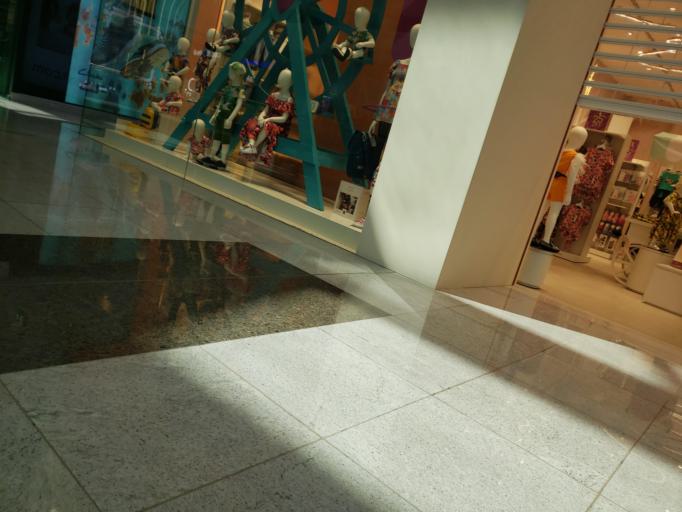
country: AE
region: Dubai
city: Dubai
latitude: 25.1958
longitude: 55.2784
